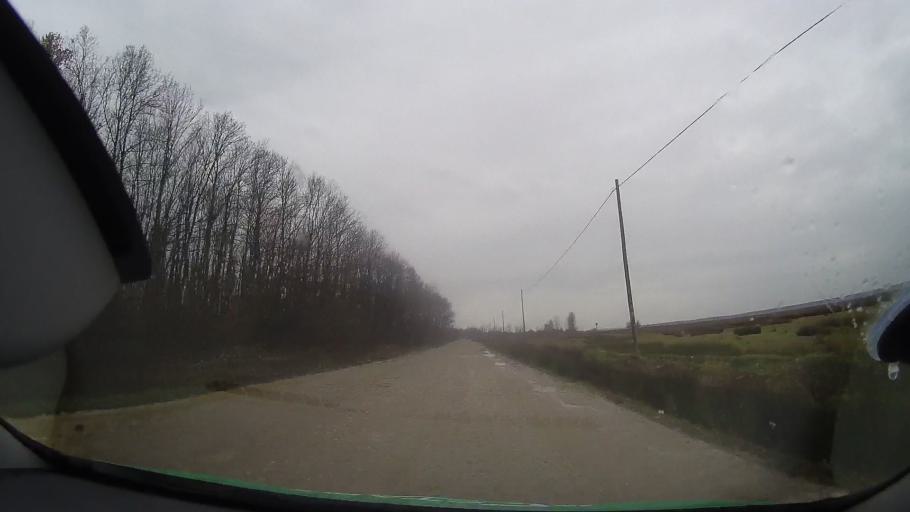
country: RO
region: Bihor
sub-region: Comuna Olcea
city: Olcea
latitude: 46.6888
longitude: 22.0054
